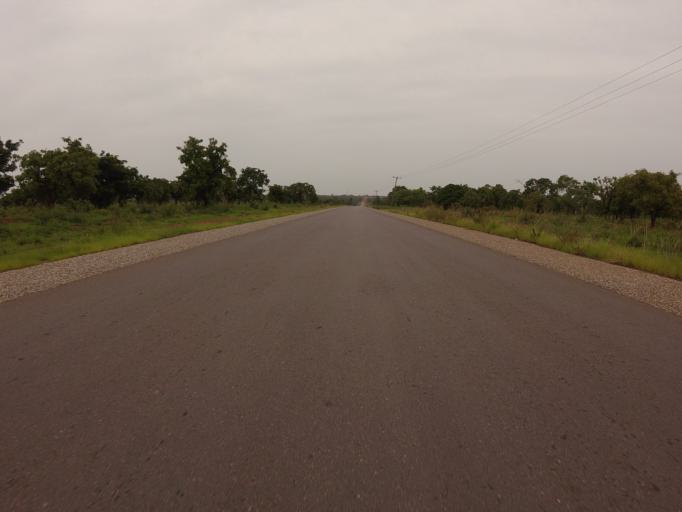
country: GH
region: Northern
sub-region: Yendi
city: Yendi
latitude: 9.2370
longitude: 0.0201
